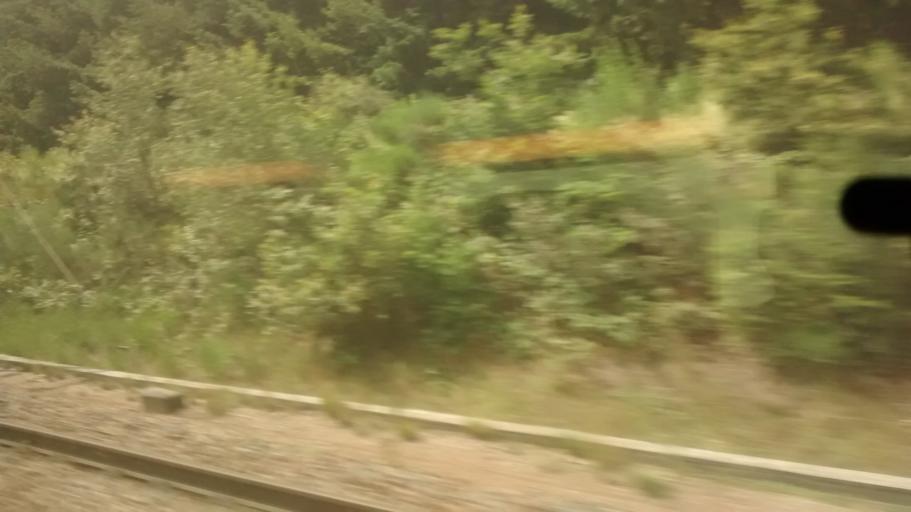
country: FR
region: Bourgogne
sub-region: Departement de Saone-et-Loire
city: Saint-Gengoux-le-National
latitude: 46.5977
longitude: 4.6084
